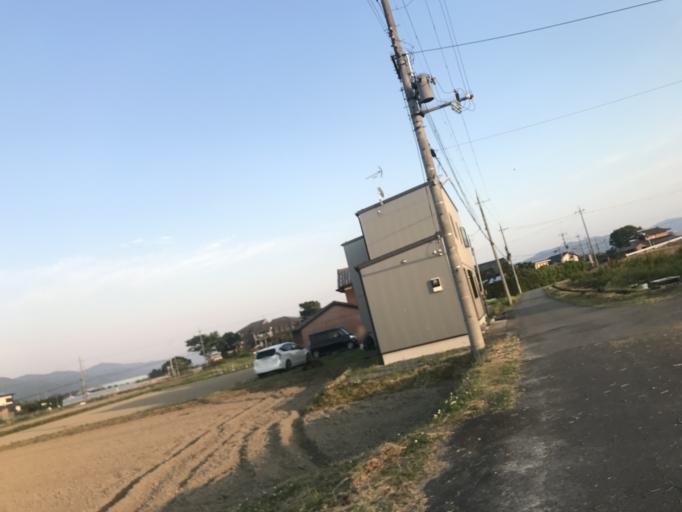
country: JP
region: Kyoto
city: Kameoka
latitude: 35.0532
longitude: 135.5530
